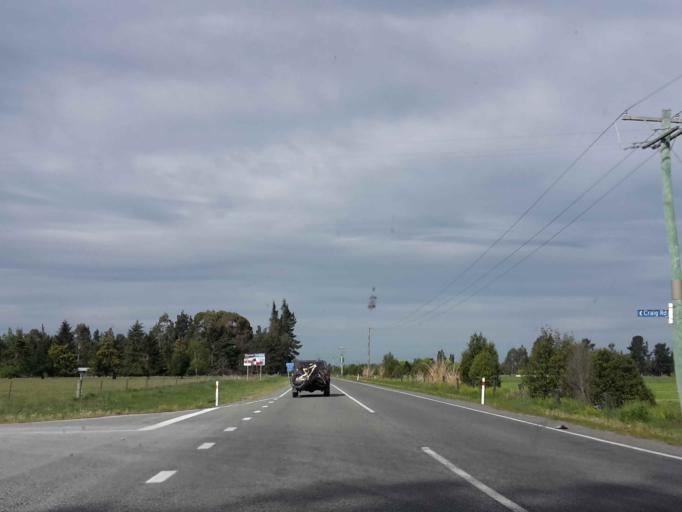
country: NZ
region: Canterbury
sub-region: Timaru District
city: Pleasant Point
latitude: -44.1133
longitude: 171.2175
